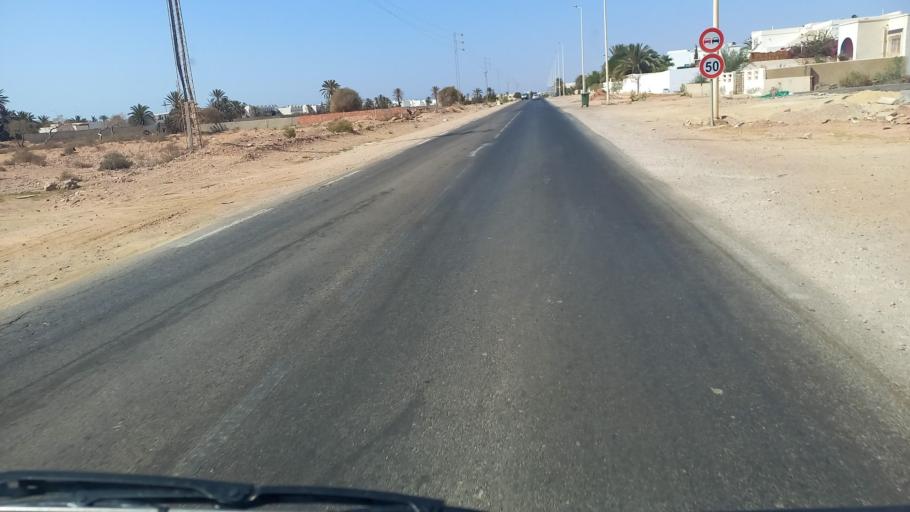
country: TN
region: Madanin
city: Midoun
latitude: 33.7645
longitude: 11.0162
